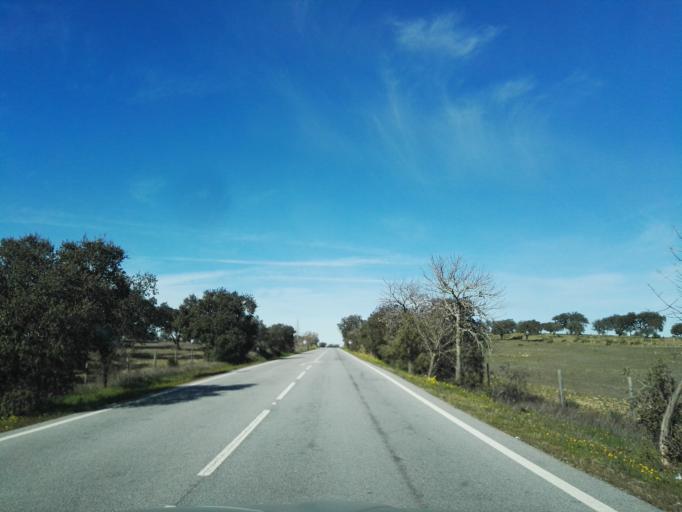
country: PT
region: Portalegre
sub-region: Arronches
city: Arronches
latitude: 39.0769
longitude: -7.2788
